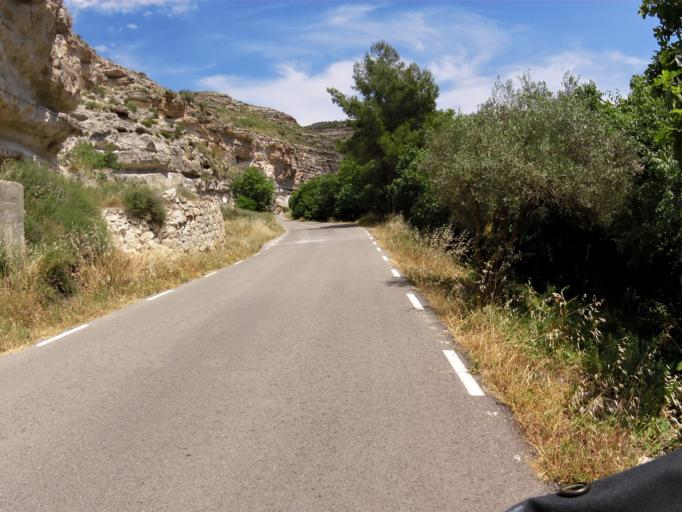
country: ES
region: Castille-La Mancha
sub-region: Provincia de Albacete
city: Jorquera
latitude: 39.1687
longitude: -1.5573
